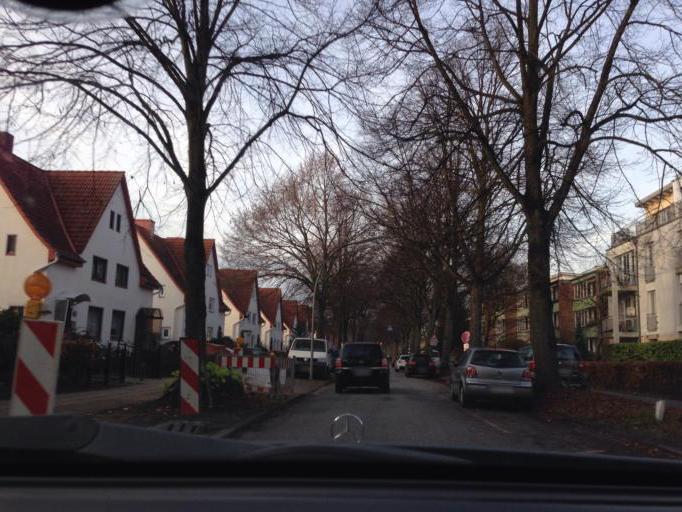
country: DE
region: Hamburg
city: Marienthal
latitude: 53.5882
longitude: 10.0843
